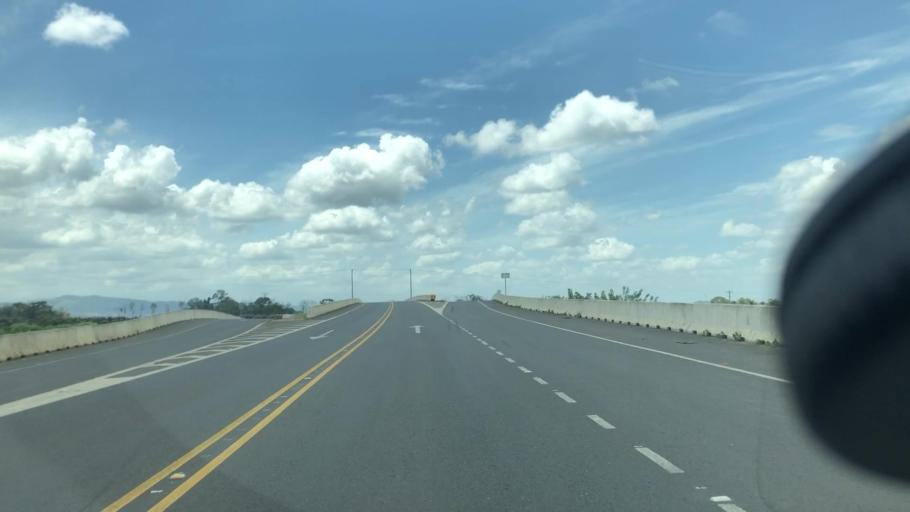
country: CR
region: Alajuela
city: Pital
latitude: 10.4345
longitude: -84.2748
